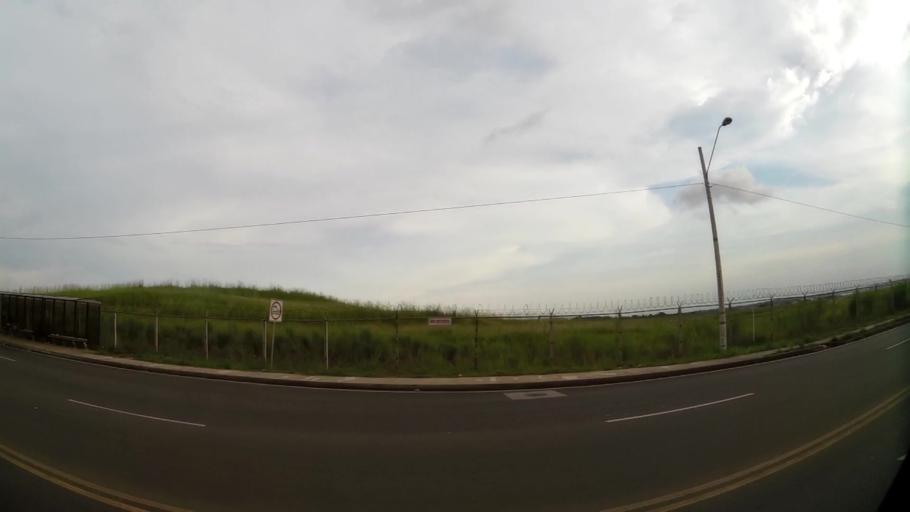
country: PA
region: Panama
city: Tocumen
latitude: 9.0913
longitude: -79.3795
